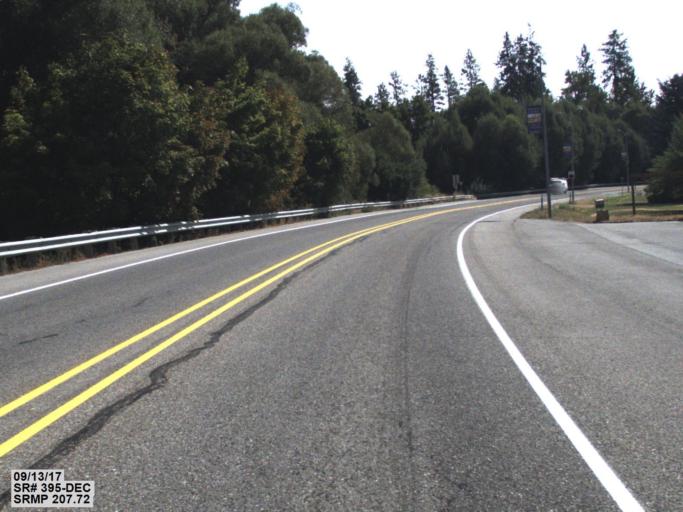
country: US
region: Washington
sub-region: Stevens County
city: Chewelah
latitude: 48.2846
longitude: -117.7166
